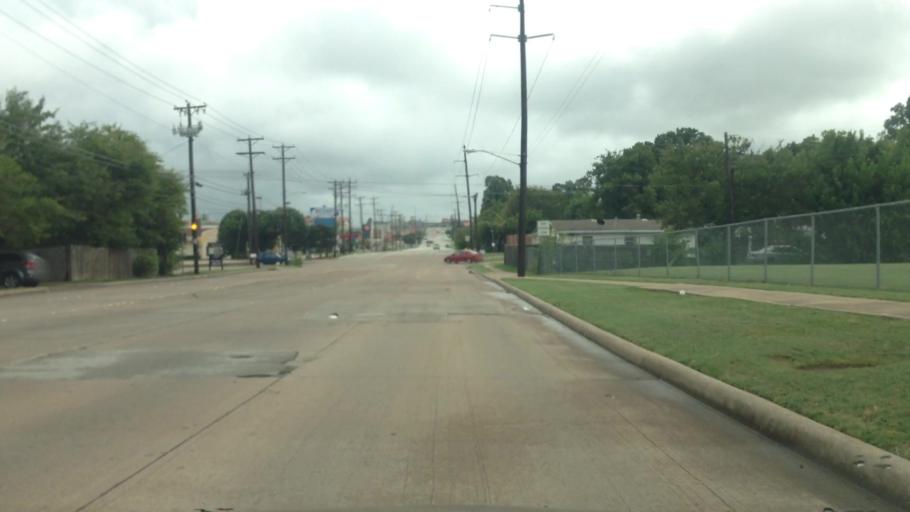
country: US
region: Texas
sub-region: Tarrant County
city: White Settlement
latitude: 32.7465
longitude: -97.4519
